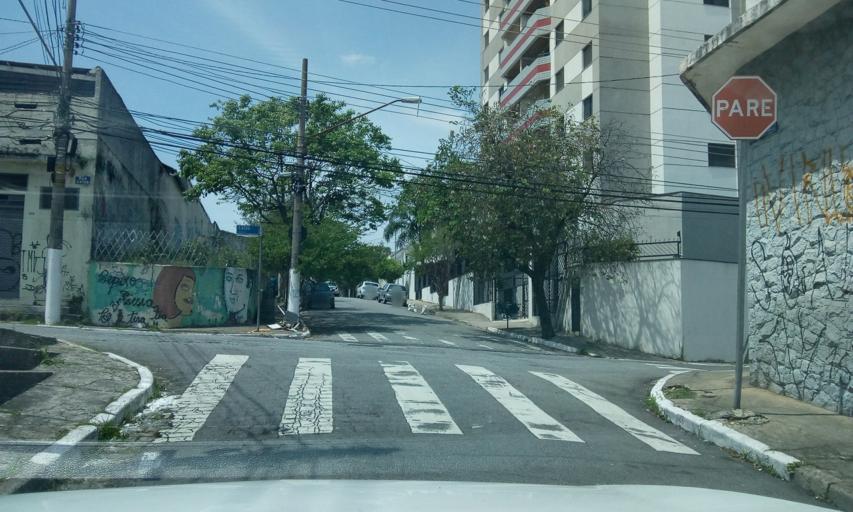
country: BR
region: Sao Paulo
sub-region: Sao Paulo
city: Sao Paulo
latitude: -23.5303
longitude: -46.7008
